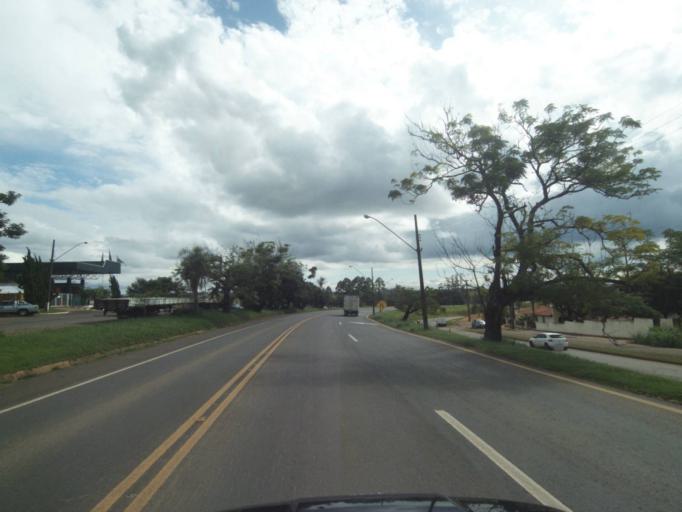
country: BR
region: Parana
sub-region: Telemaco Borba
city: Telemaco Borba
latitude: -24.3325
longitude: -50.6491
